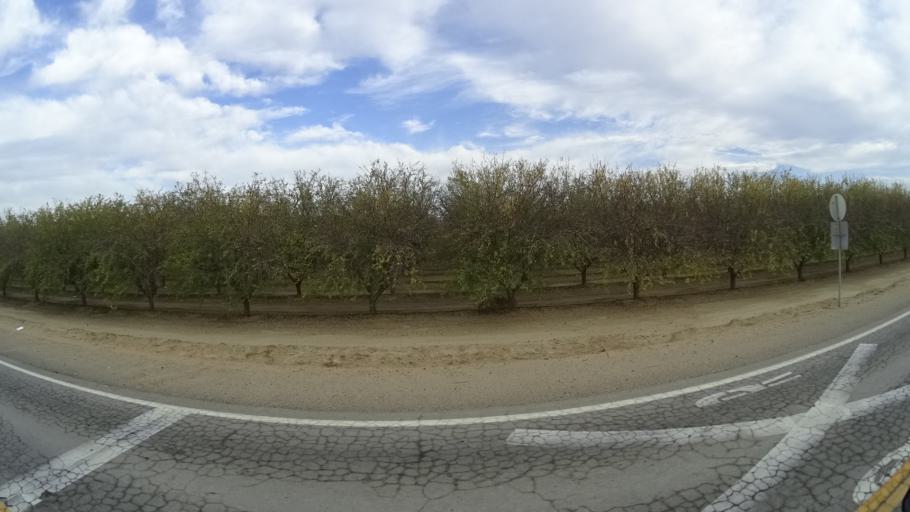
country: US
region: California
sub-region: Kern County
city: Rosedale
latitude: 35.4197
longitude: -119.1699
